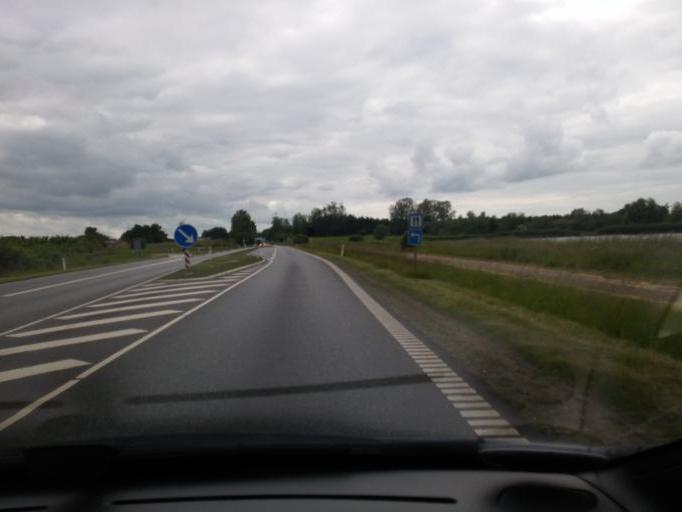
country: DK
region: Capital Region
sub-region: Hillerod Kommune
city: Hillerod
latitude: 55.9552
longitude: 12.2637
